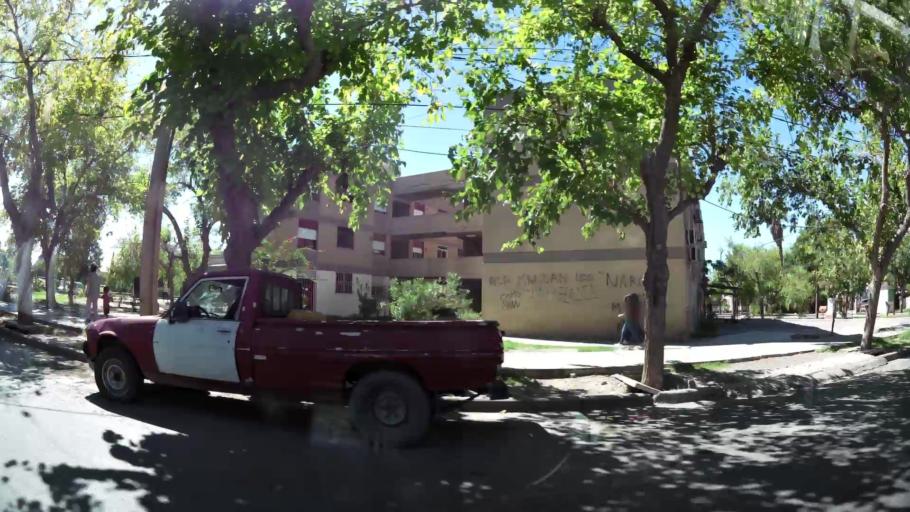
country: AR
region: San Juan
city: Villa Krause
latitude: -31.5558
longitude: -68.5224
